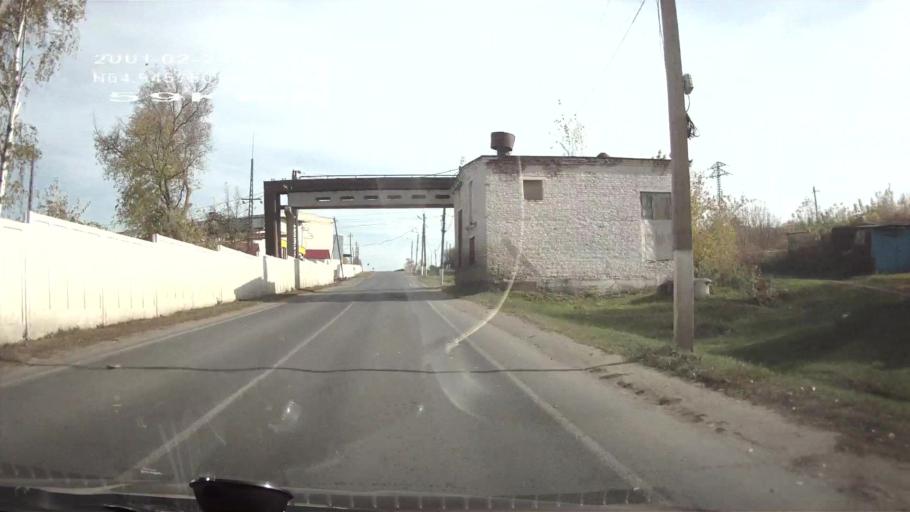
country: RU
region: Mordoviya
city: Turgenevo
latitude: 54.8458
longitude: 46.3404
